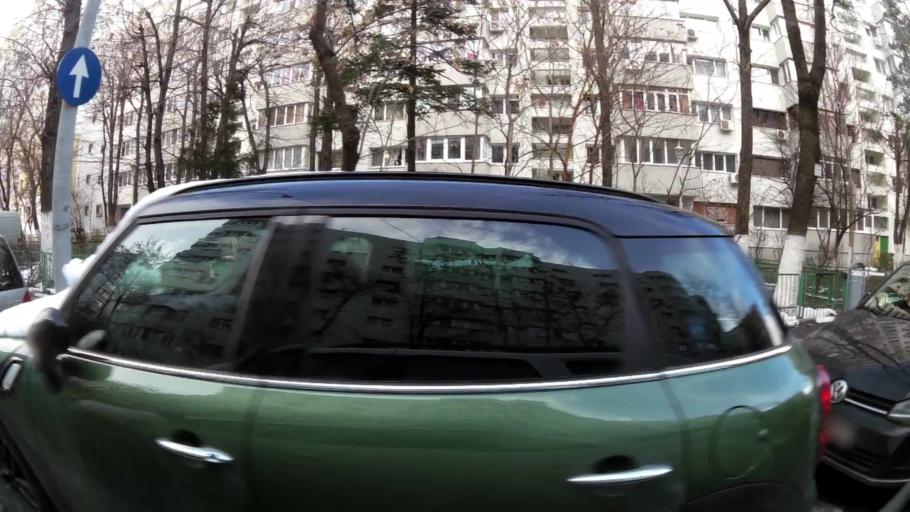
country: RO
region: Bucuresti
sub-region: Municipiul Bucuresti
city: Bucharest
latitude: 44.4207
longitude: 26.1429
